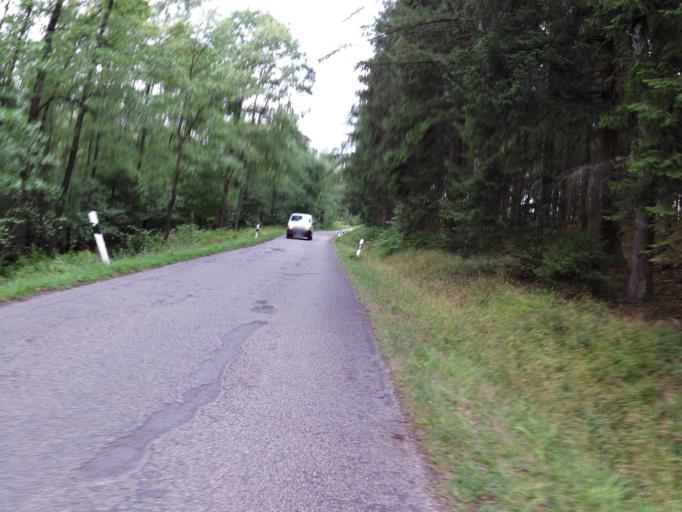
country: DE
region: North Rhine-Westphalia
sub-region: Regierungsbezirk Koln
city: Hurtgenwald
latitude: 50.7564
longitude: 6.3174
